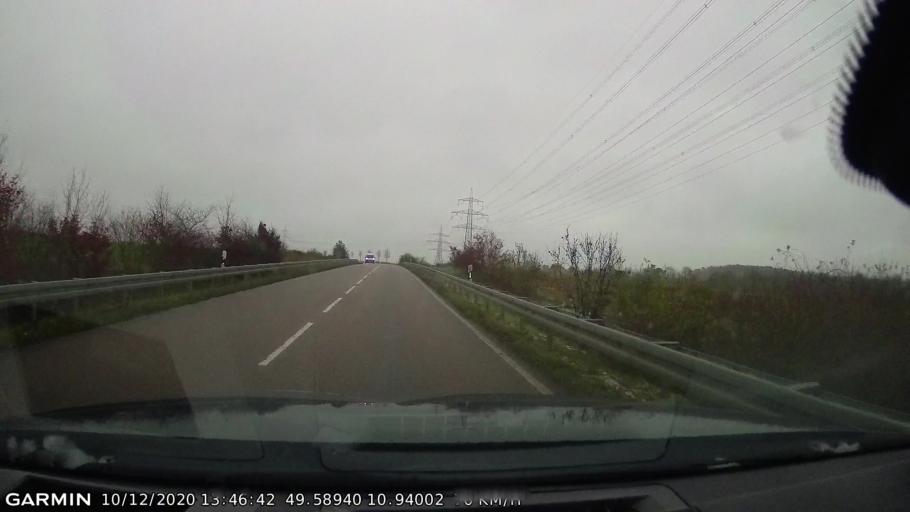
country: DE
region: Bavaria
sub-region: Regierungsbezirk Mittelfranken
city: Hessdorf
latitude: 49.5893
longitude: 10.9399
